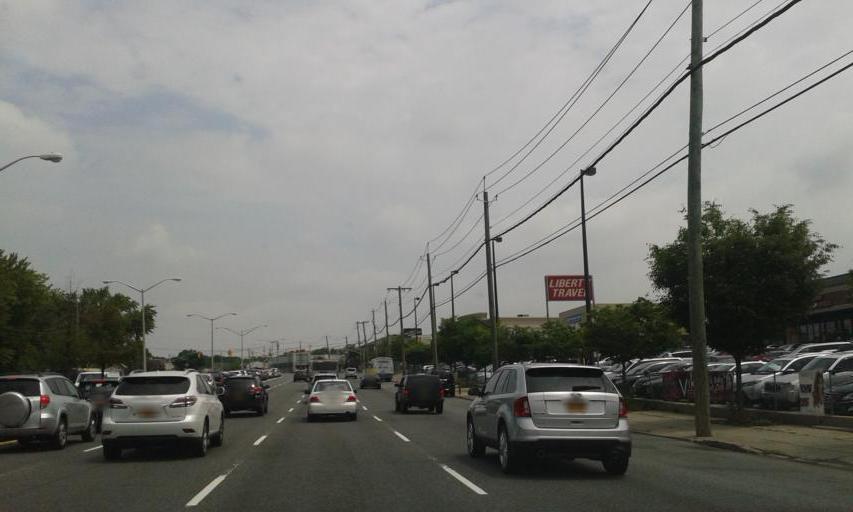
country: US
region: New York
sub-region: Richmond County
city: Bloomfield
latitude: 40.5911
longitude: -74.1651
